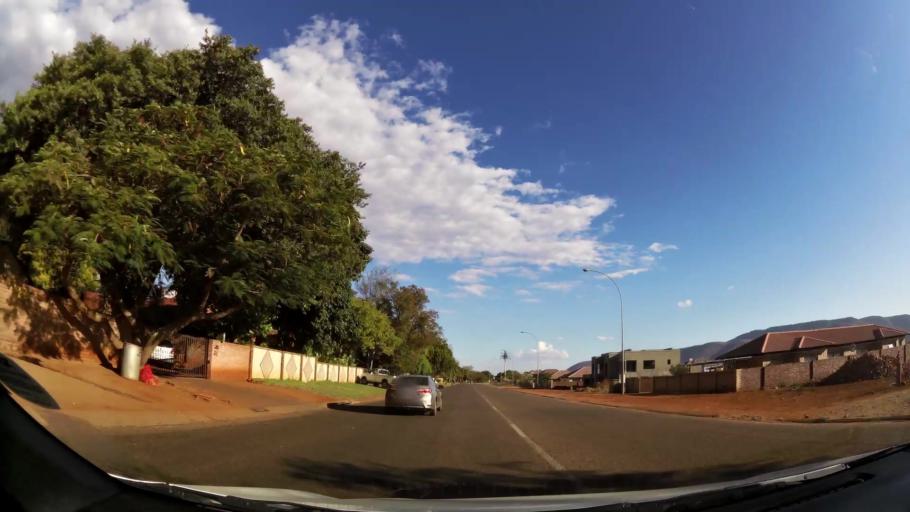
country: ZA
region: Limpopo
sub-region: Waterberg District Municipality
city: Mokopane
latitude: -24.2008
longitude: 29.0021
